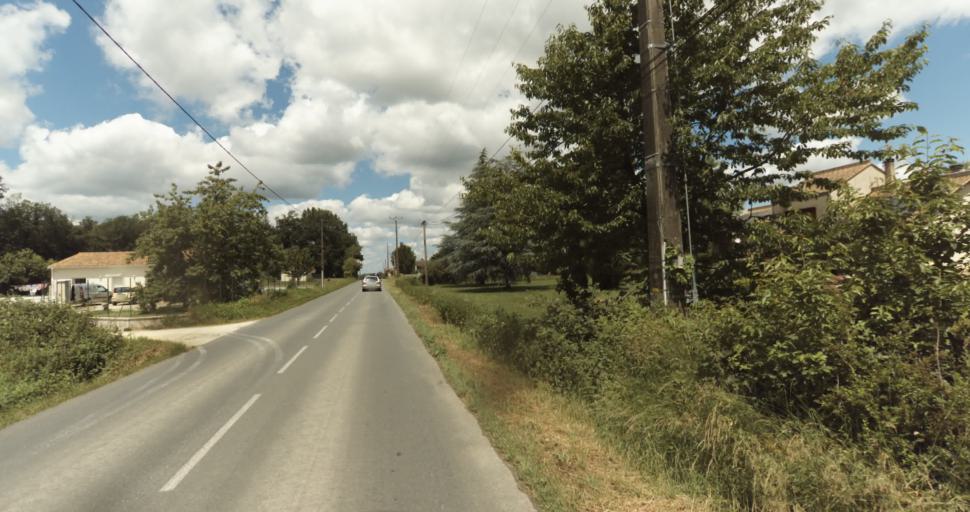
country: FR
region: Aquitaine
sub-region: Departement de la Dordogne
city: Beaumont-du-Perigord
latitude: 44.7318
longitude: 0.7552
